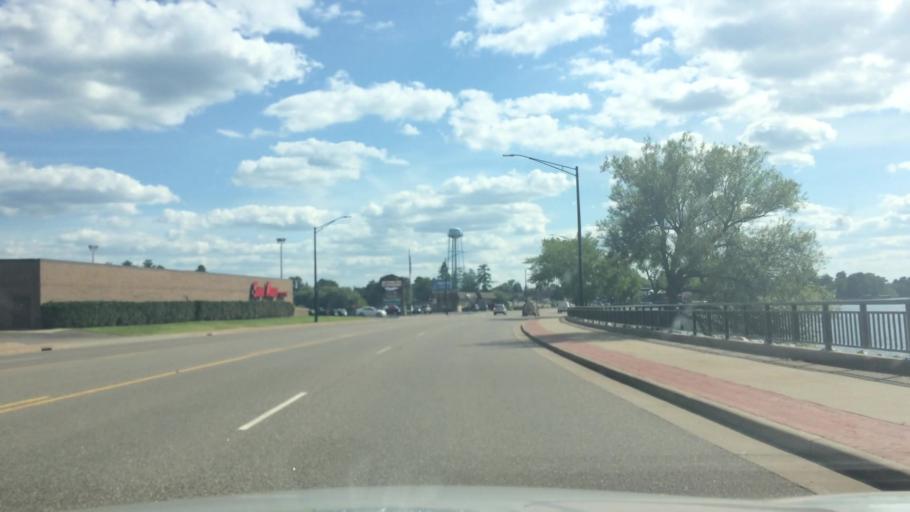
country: US
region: Wisconsin
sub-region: Vilas County
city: Lac du Flambeau
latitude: 45.8777
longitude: -89.7040
